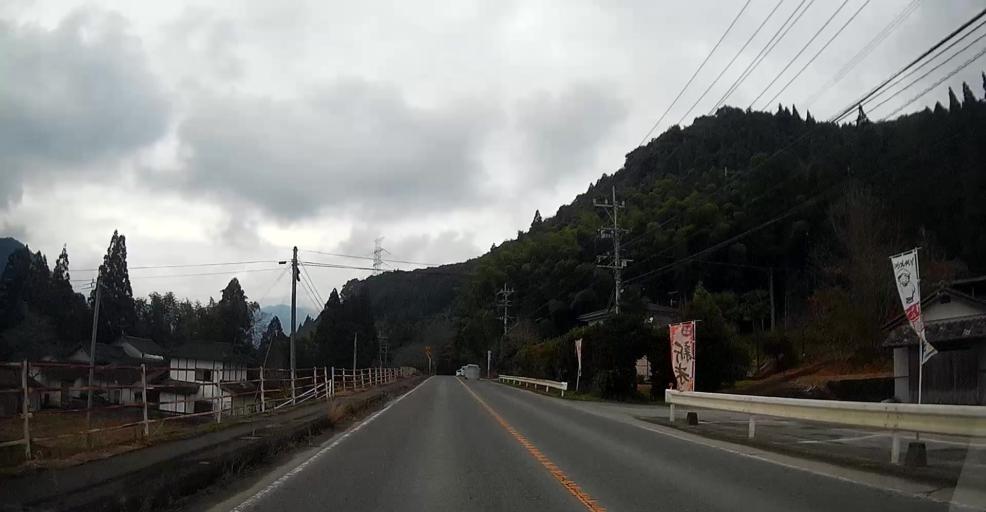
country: JP
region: Kumamoto
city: Matsubase
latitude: 32.6303
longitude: 130.8085
